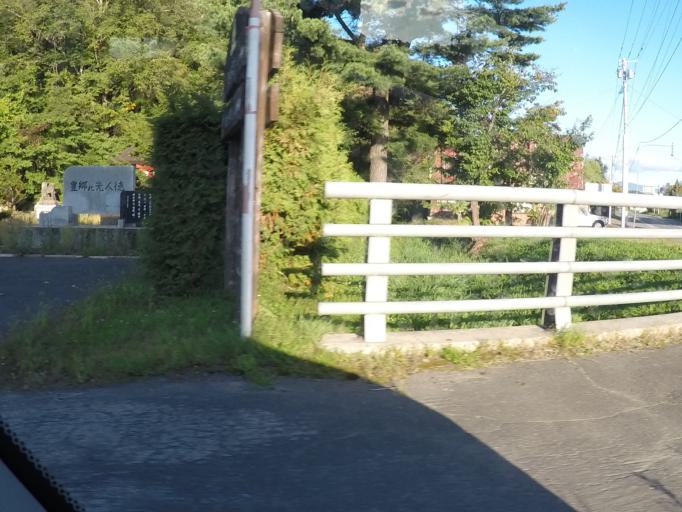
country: JP
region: Hokkaido
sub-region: Asahikawa-shi
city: Asahikawa
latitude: 43.6153
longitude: 142.4798
